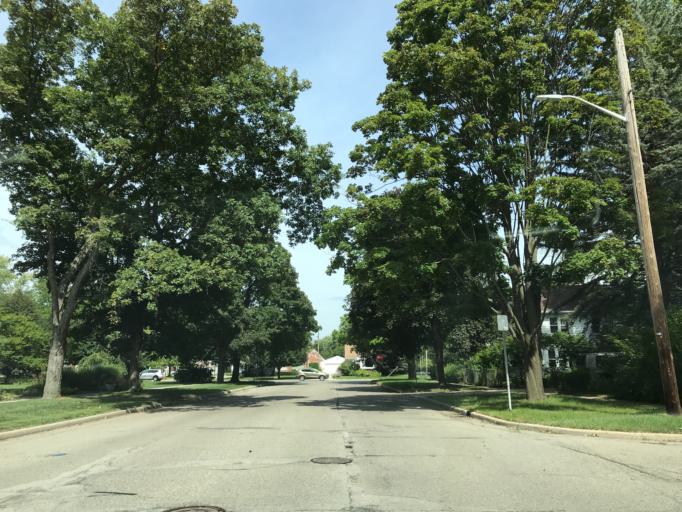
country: US
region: Michigan
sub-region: Washtenaw County
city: Ypsilanti
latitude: 42.2445
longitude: -83.6325
